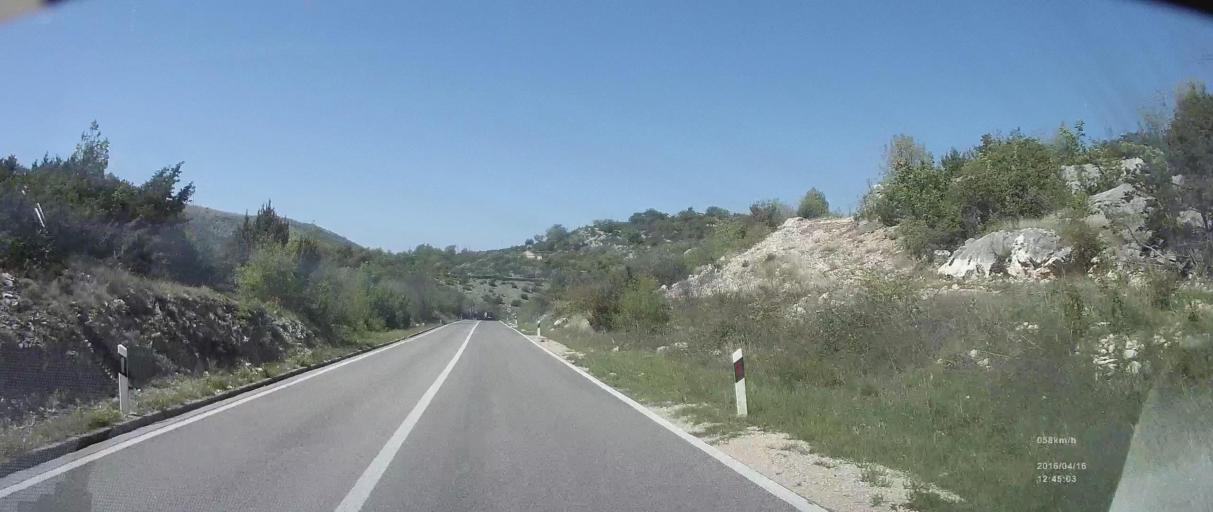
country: HR
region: Sibensko-Kniniska
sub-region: Grad Sibenik
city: Brodarica
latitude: 43.6470
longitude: 16.0606
